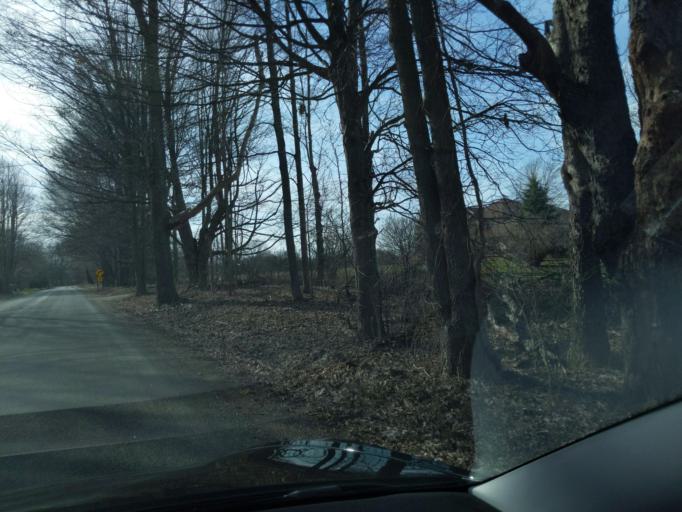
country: US
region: Michigan
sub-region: Ingham County
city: Okemos
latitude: 42.6763
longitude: -84.3801
